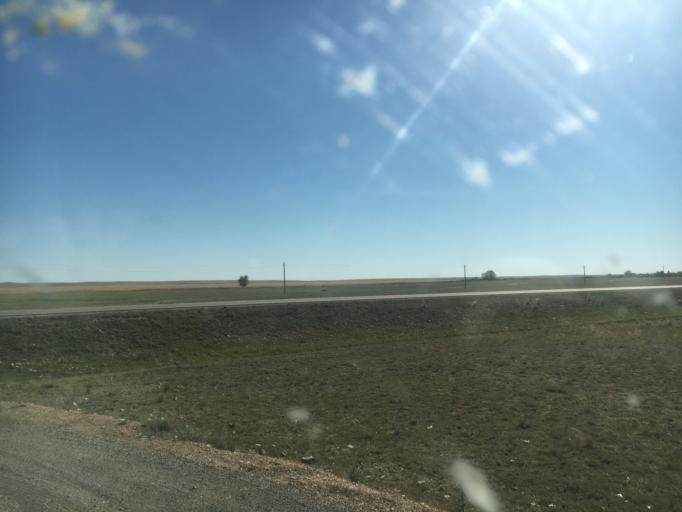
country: RU
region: Orenburg
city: Dombarovskiy
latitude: 50.0714
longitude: 59.6231
